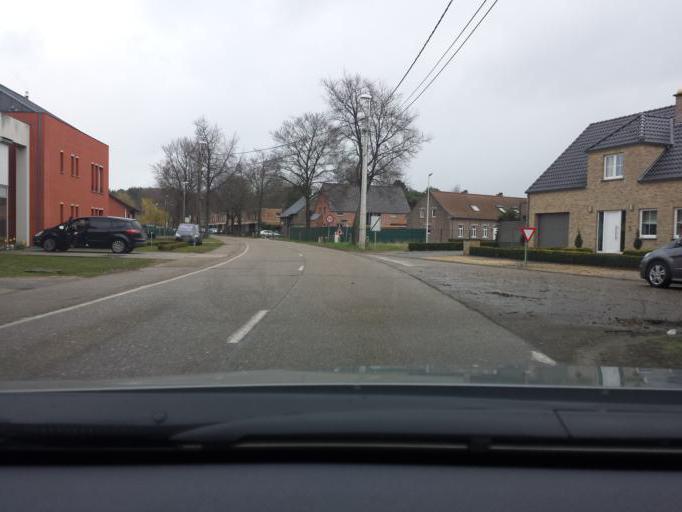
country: BE
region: Flanders
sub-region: Provincie Limburg
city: Lummen
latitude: 50.9781
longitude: 5.1765
